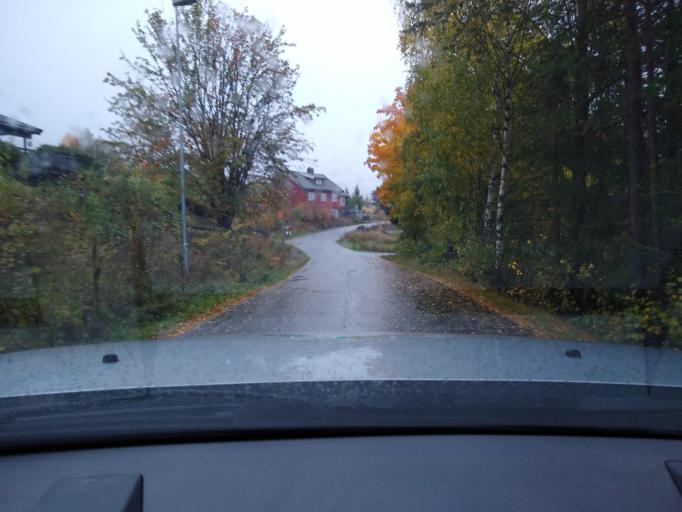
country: NO
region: Oppland
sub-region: Ringebu
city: Ringebu
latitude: 61.5330
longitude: 10.1457
